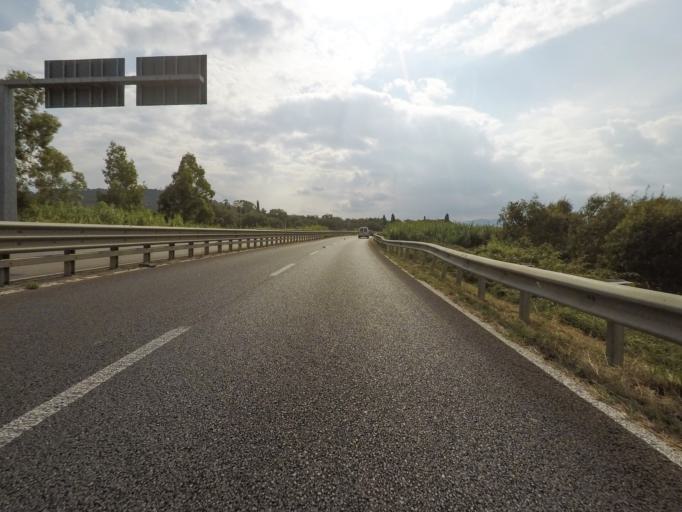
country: IT
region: Tuscany
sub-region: Provincia di Grosseto
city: Grosseto
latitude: 42.7131
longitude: 11.1445
